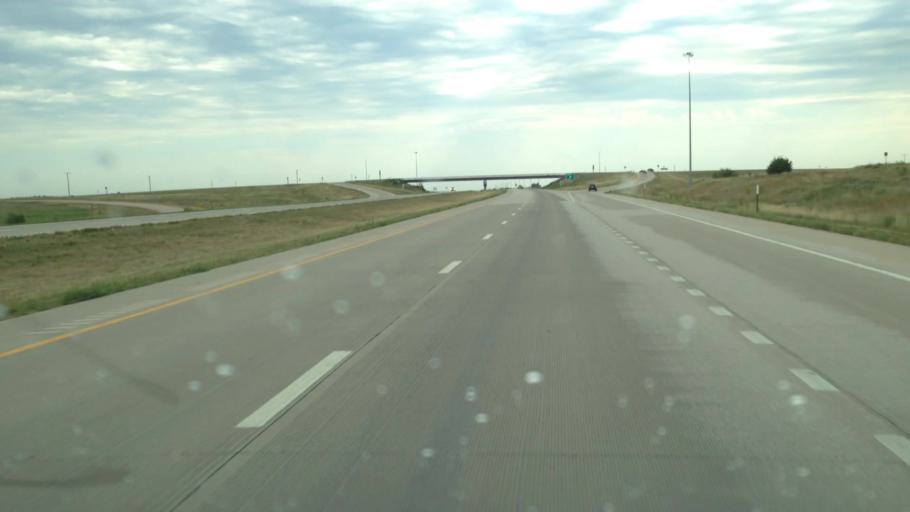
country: US
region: Kansas
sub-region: Douglas County
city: Baldwin City
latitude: 38.8378
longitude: -95.2689
